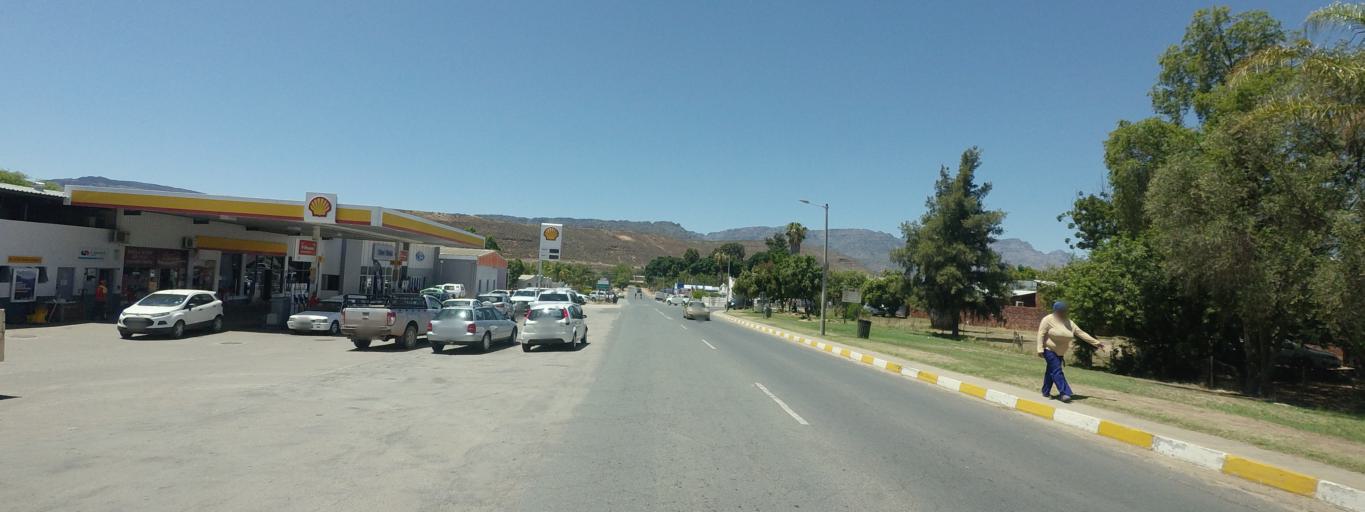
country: ZA
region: Western Cape
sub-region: West Coast District Municipality
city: Clanwilliam
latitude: -32.1757
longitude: 18.8916
